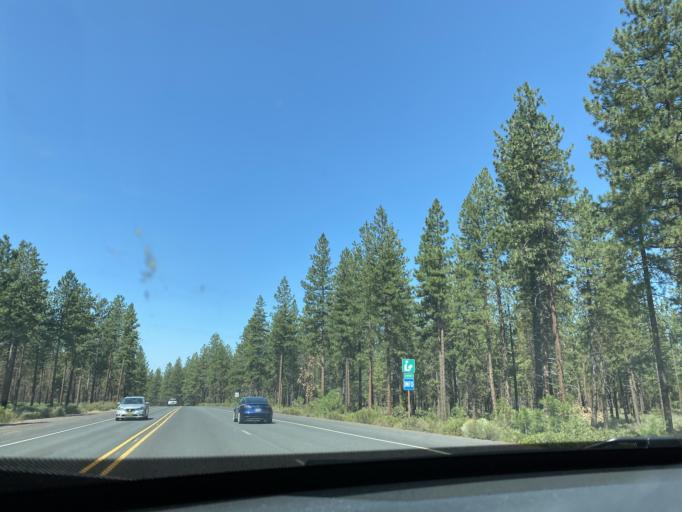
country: US
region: Oregon
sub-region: Deschutes County
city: Sunriver
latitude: 43.8703
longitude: -121.4068
